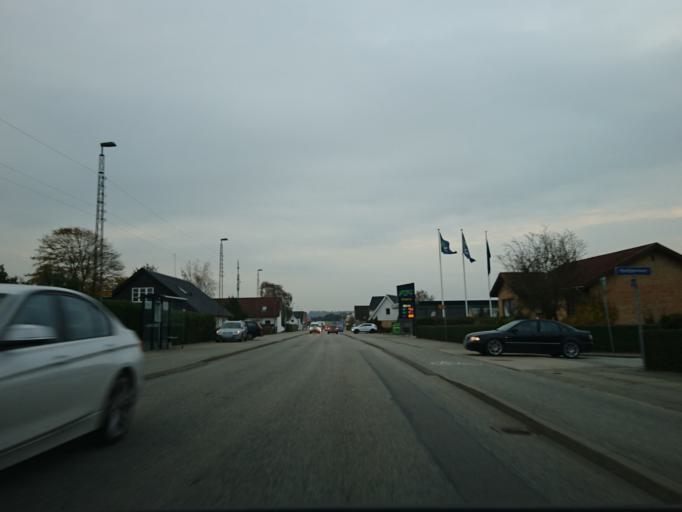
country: DK
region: North Denmark
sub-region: Alborg Kommune
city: Aalborg
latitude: 57.0108
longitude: 9.9259
